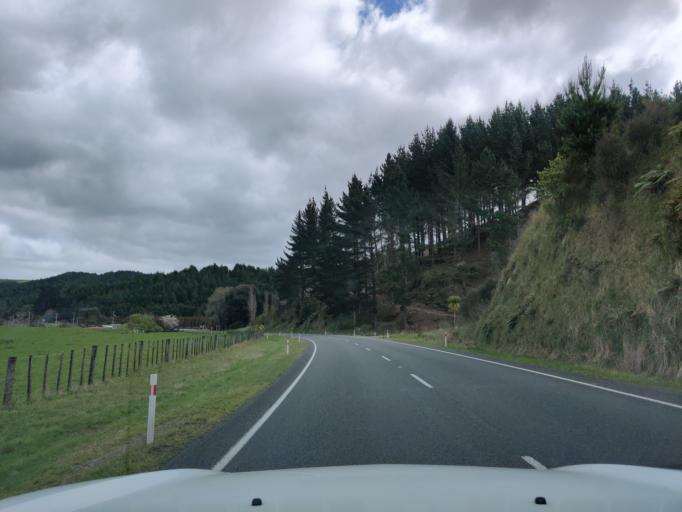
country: NZ
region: Manawatu-Wanganui
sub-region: Wanganui District
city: Wanganui
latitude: -39.8468
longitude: 175.1310
